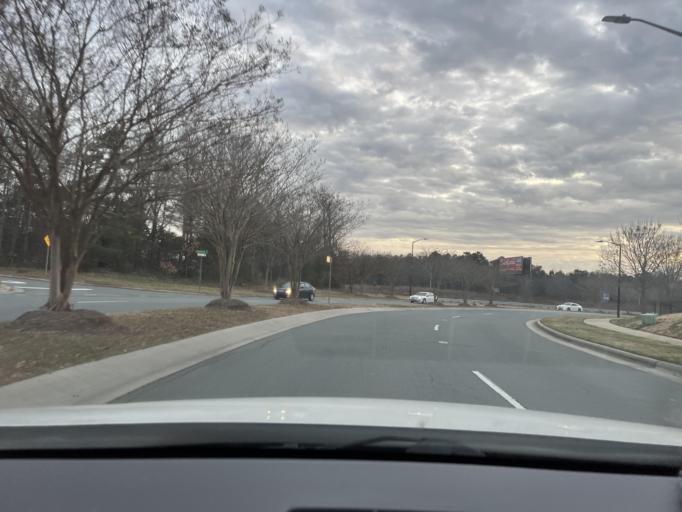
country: US
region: North Carolina
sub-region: Alamance County
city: Elon
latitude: 36.0690
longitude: -79.5052
